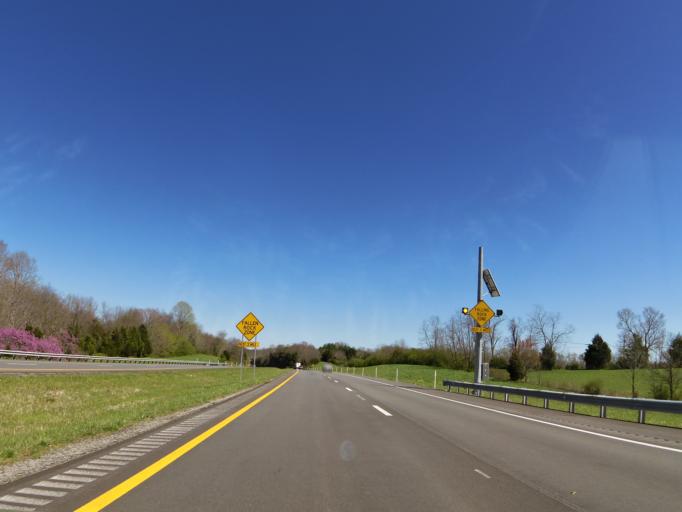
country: US
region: Kentucky
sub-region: Pulaski County
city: Somerset
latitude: 37.0963
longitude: -84.7181
